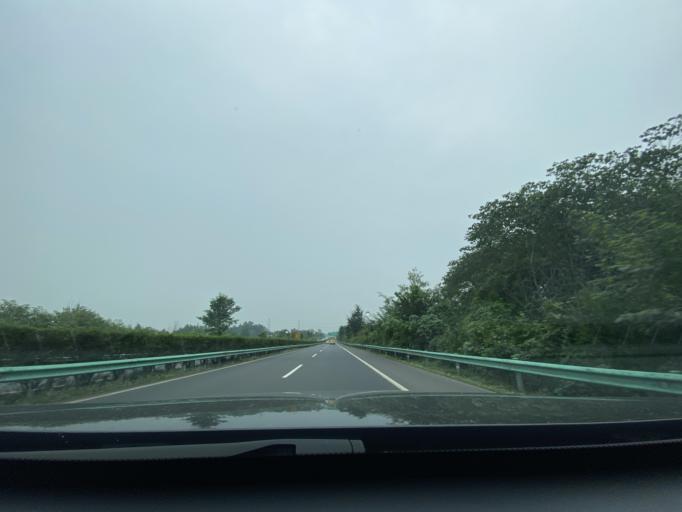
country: CN
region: Sichuan
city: Longquan
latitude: 30.3256
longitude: 104.1206
